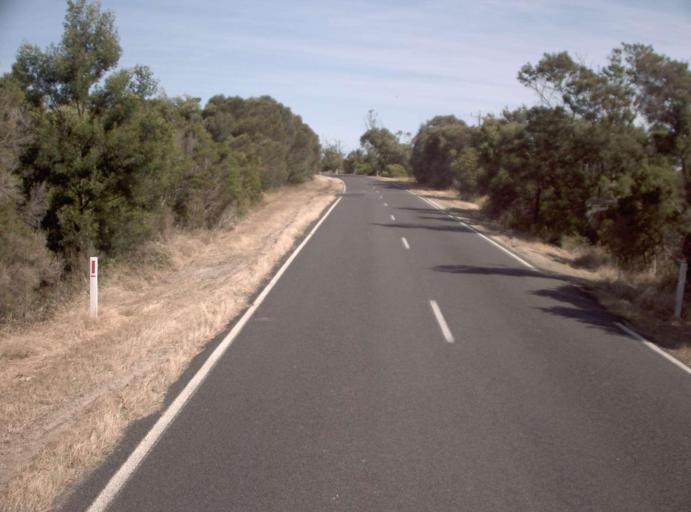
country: AU
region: Victoria
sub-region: Wellington
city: Sale
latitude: -38.3350
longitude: 147.1631
